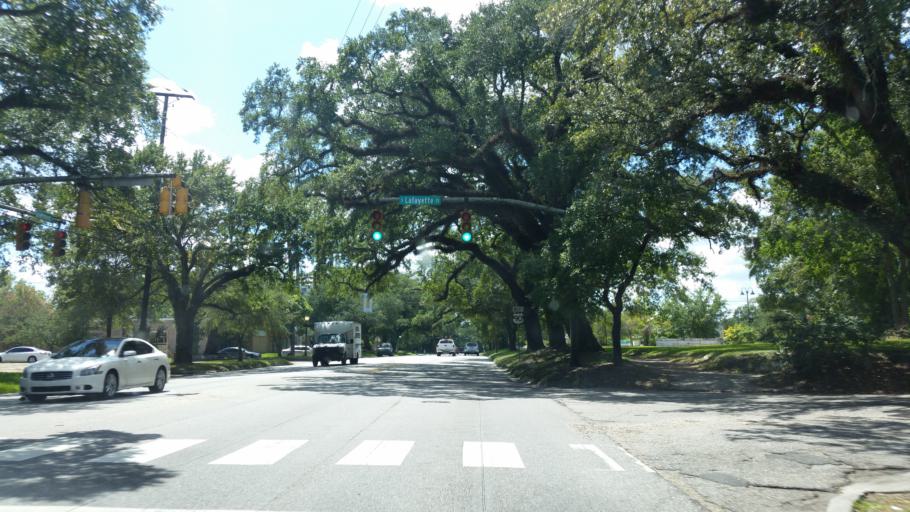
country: US
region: Alabama
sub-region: Mobile County
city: Mobile
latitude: 30.6809
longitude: -88.0714
